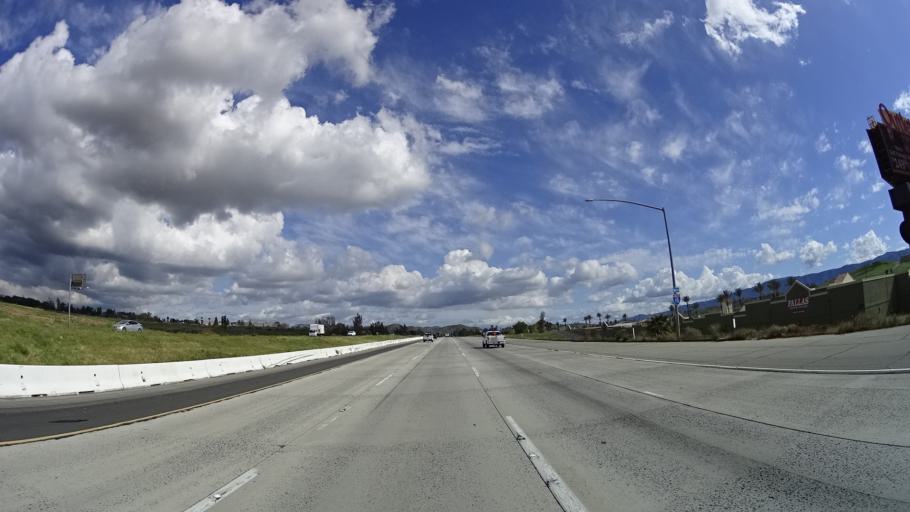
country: US
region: California
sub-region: Riverside County
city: Lake Elsinore
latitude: 33.7039
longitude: -117.3545
